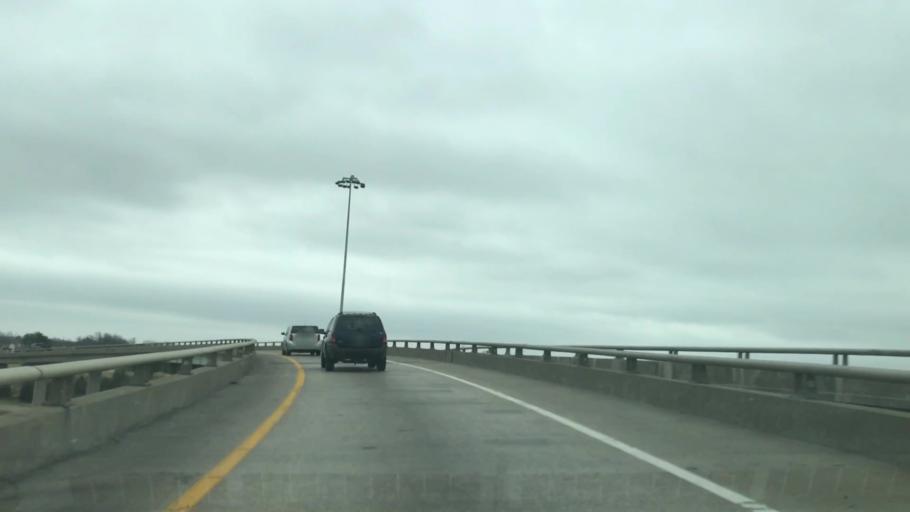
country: US
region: Texas
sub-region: Dallas County
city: Mesquite
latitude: 32.8232
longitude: -96.6300
